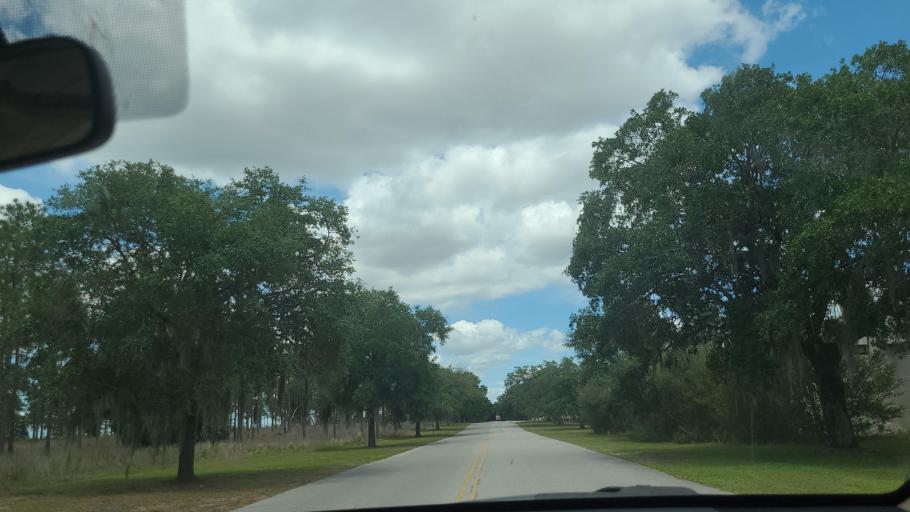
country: US
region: Florida
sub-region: Polk County
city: Lake Wales
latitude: 27.9142
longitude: -81.5660
